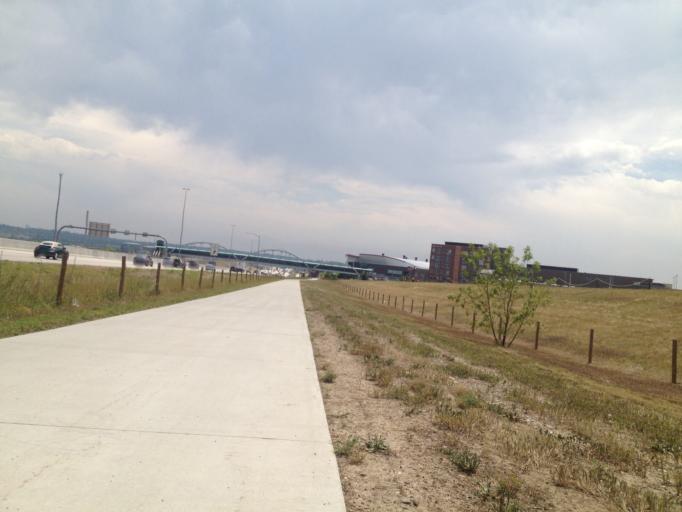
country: US
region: Colorado
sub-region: Broomfield County
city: Broomfield
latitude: 39.9095
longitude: -105.0876
